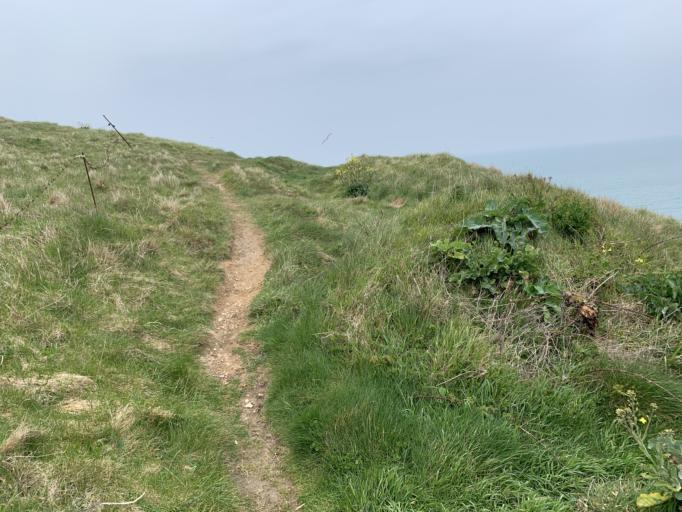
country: FR
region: Haute-Normandie
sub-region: Departement de la Seine-Maritime
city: Etretat
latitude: 49.6886
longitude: 0.1678
